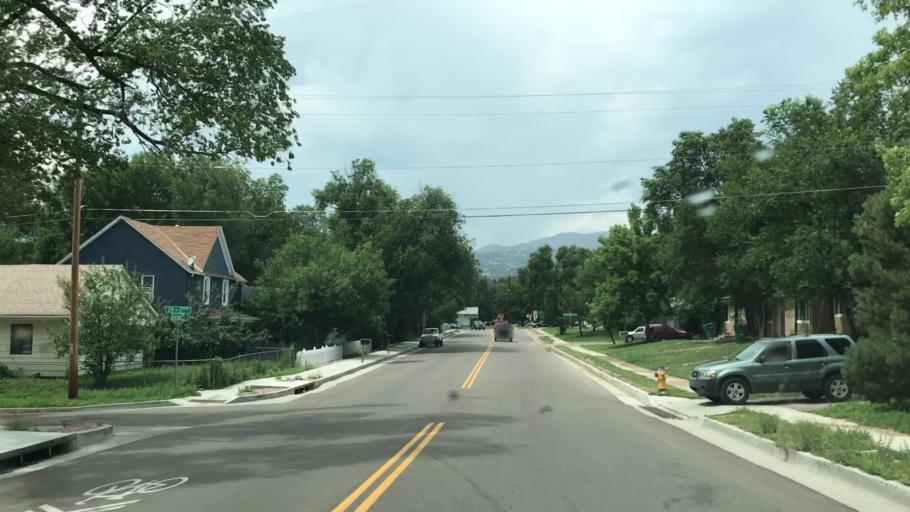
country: US
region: Colorado
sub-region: El Paso County
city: Colorado Springs
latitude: 38.8542
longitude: -104.8651
